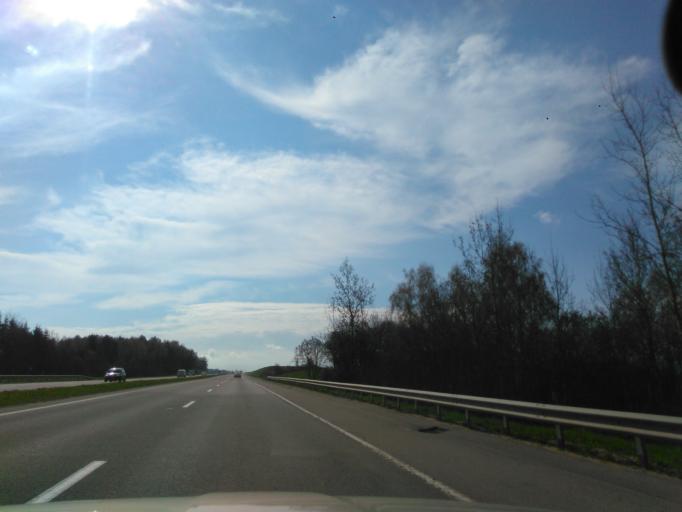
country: BY
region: Minsk
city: Novosel'ye
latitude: 53.9369
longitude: 27.1372
